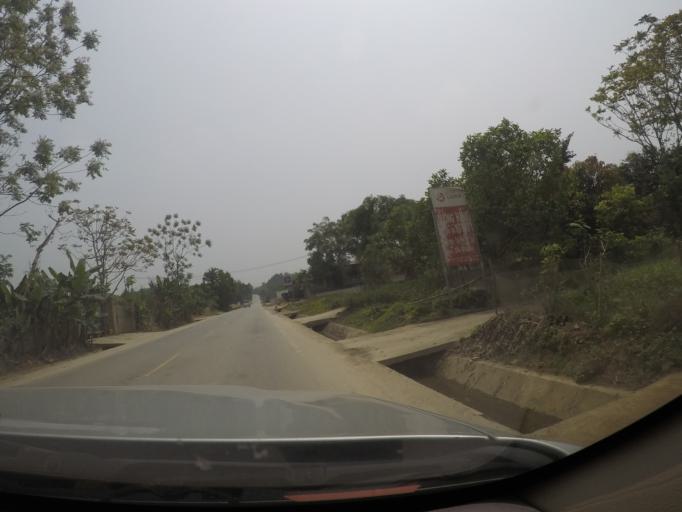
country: VN
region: Thanh Hoa
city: Thi Tran Yen Cat
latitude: 19.7203
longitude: 105.4308
